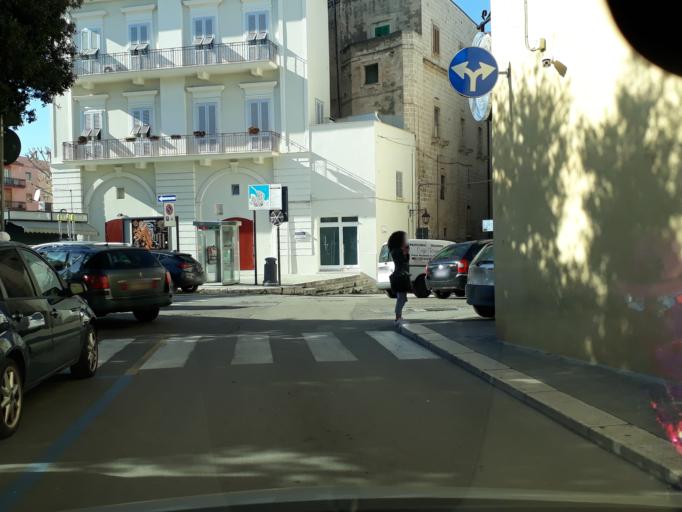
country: IT
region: Apulia
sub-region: Provincia di Bari
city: Monopoli
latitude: 40.9508
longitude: 17.3026
